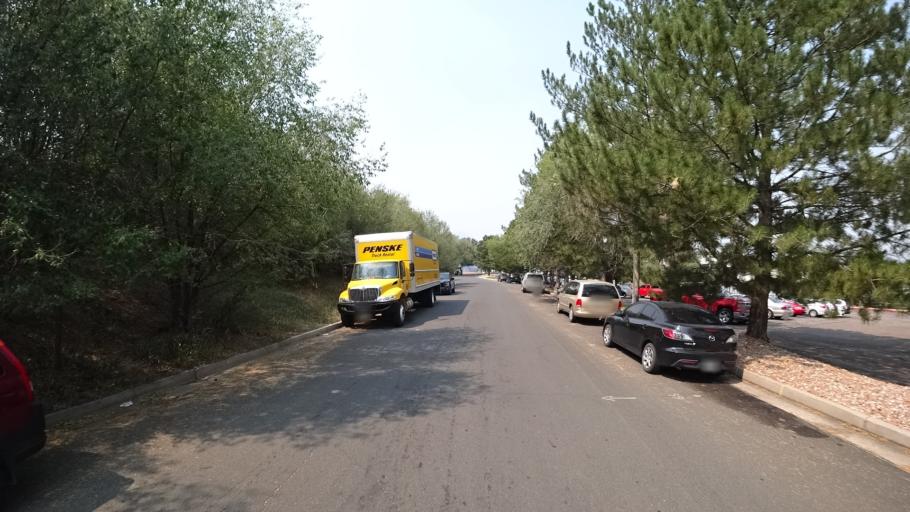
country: US
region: Colorado
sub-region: El Paso County
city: Colorado Springs
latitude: 38.8139
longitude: -104.8341
